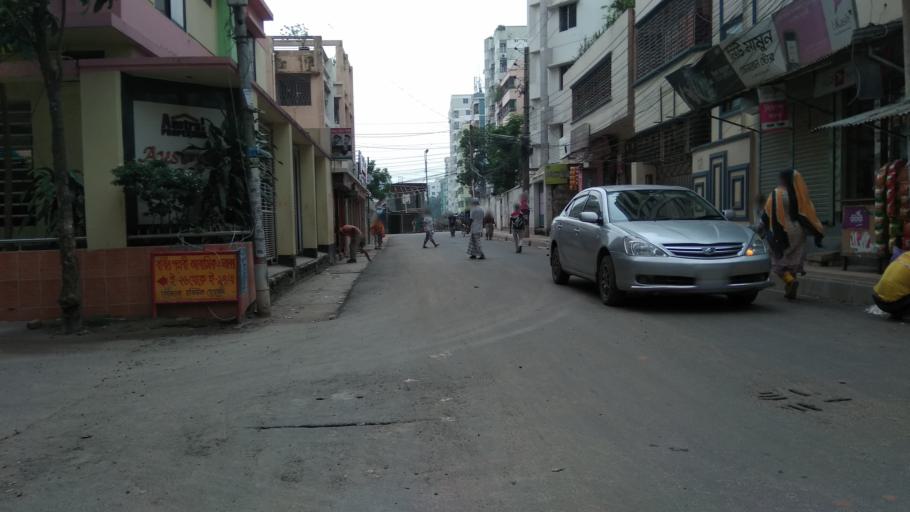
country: BD
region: Dhaka
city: Tungi
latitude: 23.8238
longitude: 90.3595
